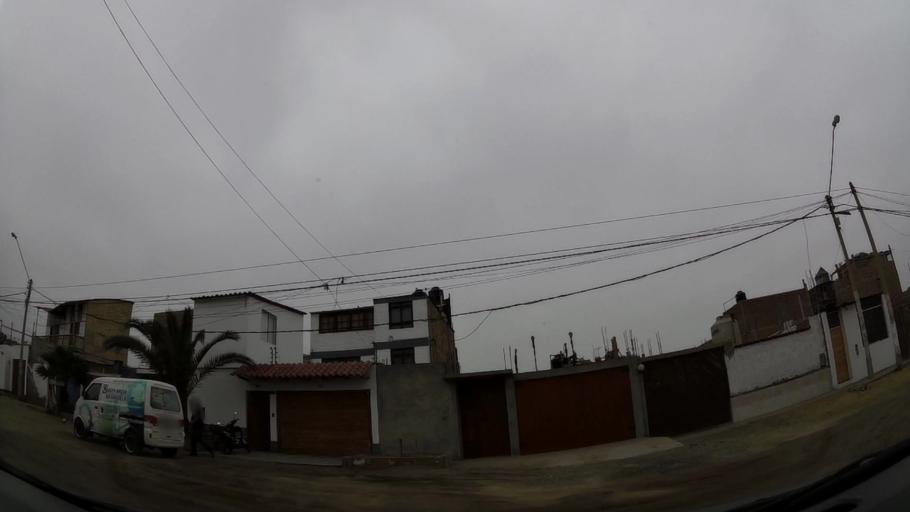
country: PE
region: Lima
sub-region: Lima
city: Punta Hermosa
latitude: -12.3316
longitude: -76.8256
